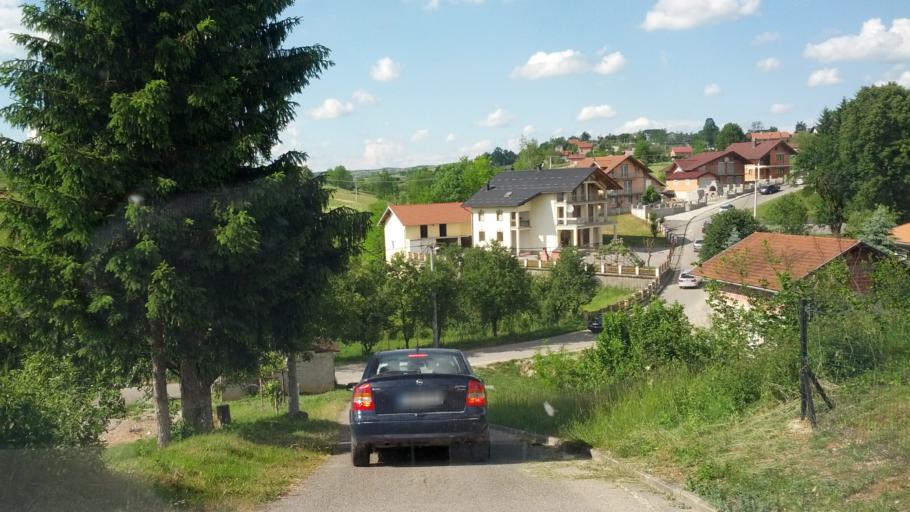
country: BA
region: Federation of Bosnia and Herzegovina
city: Ostrozac
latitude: 44.9196
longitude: 15.9530
